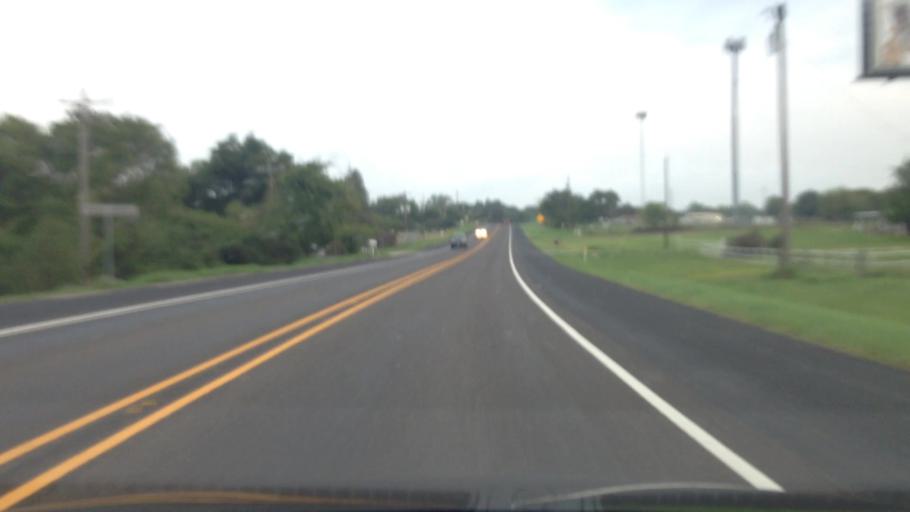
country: US
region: Texas
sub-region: Johnson County
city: Burleson
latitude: 32.4943
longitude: -97.3357
